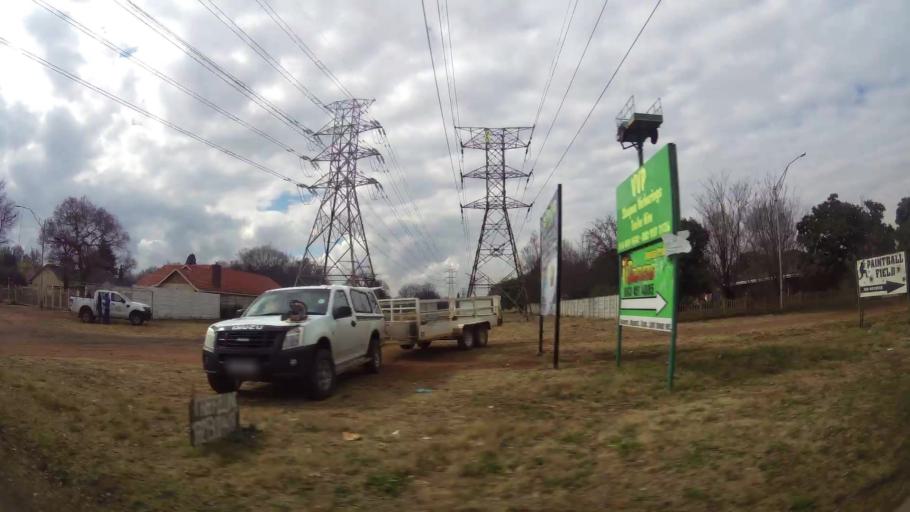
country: ZA
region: Gauteng
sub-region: Sedibeng District Municipality
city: Vereeniging
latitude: -26.6456
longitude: 27.9704
